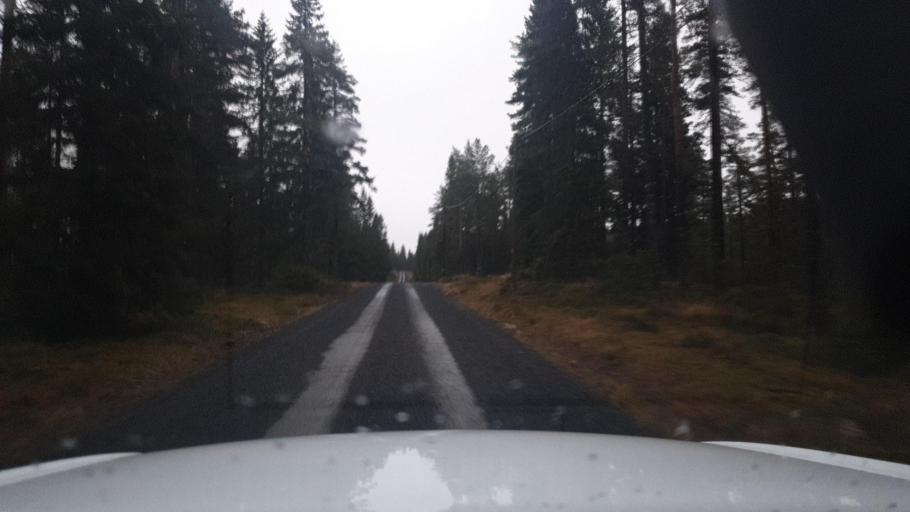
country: SE
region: Vaermland
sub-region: Torsby Kommun
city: Torsby
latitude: 60.1676
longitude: 12.6209
